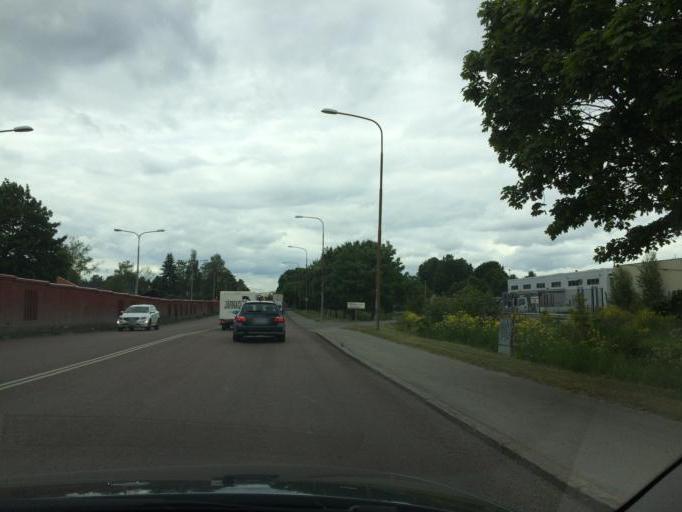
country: SE
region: Stockholm
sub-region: Stockholms Kommun
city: Kista
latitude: 59.3743
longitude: 17.9164
